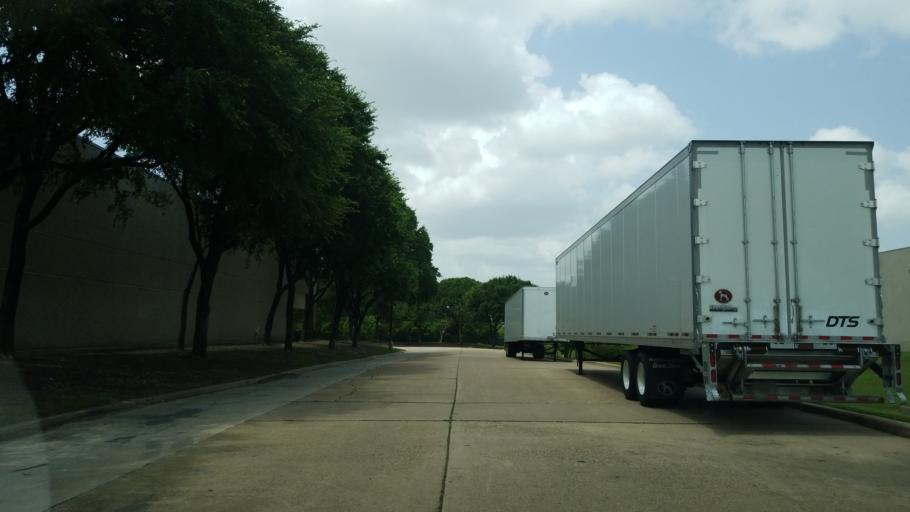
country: US
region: Texas
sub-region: Dallas County
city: Cockrell Hill
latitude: 32.7720
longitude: -96.8916
